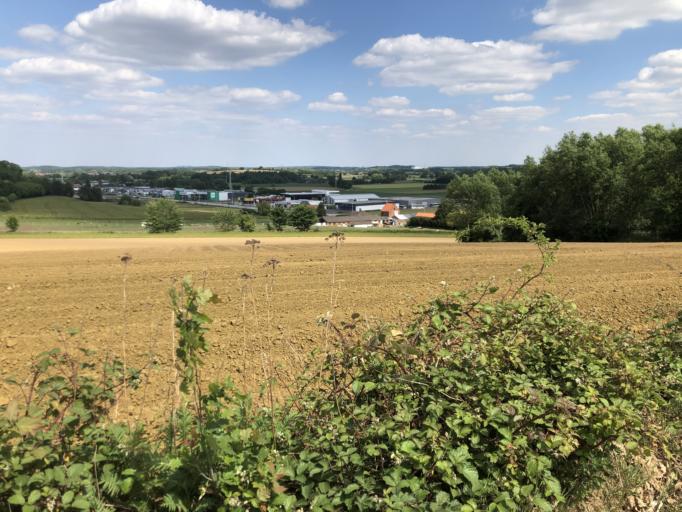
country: BE
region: Flanders
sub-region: Provincie Vlaams-Brabant
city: Diest
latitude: 50.9636
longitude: 5.0224
